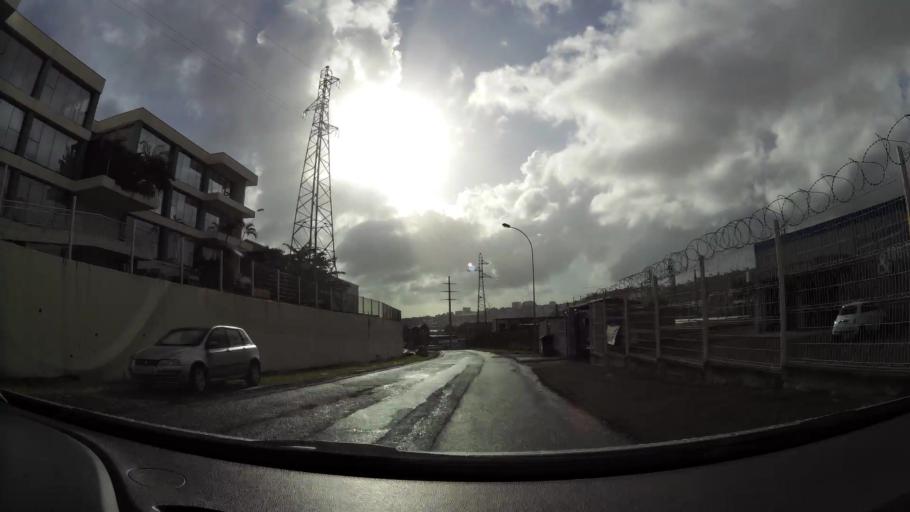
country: MQ
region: Martinique
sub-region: Martinique
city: Fort-de-France
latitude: 14.6171
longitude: -61.0433
